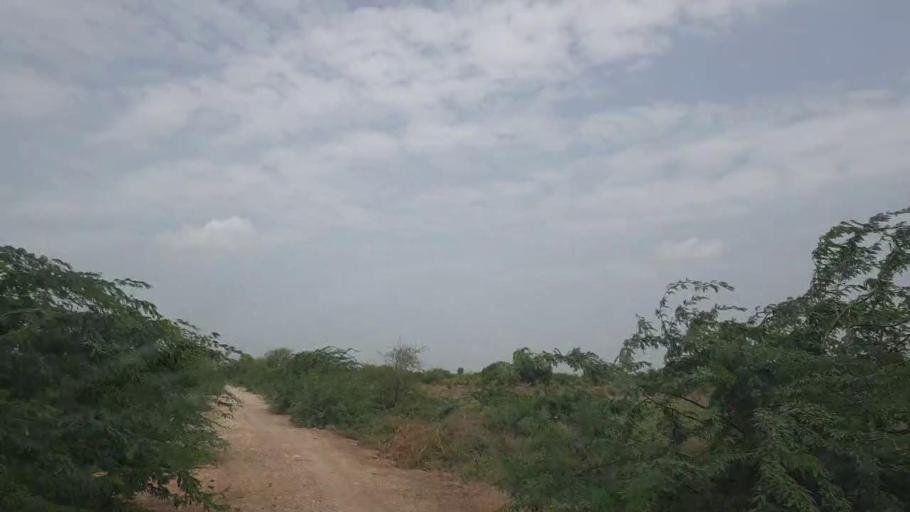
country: PK
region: Sindh
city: Tando Bago
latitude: 24.9283
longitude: 69.0988
